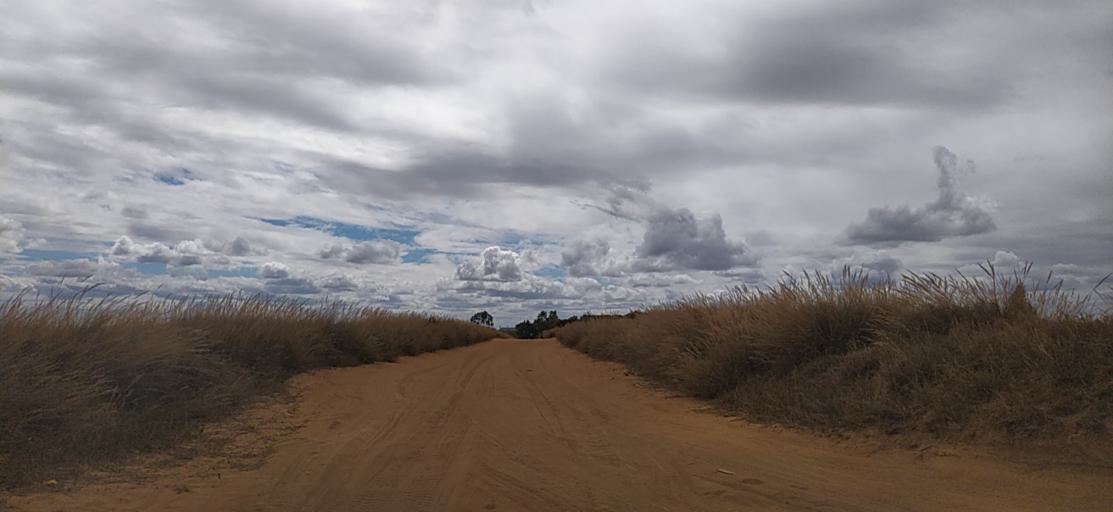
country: MG
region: Alaotra Mangoro
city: Ambatondrazaka
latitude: -17.9025
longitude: 48.2581
